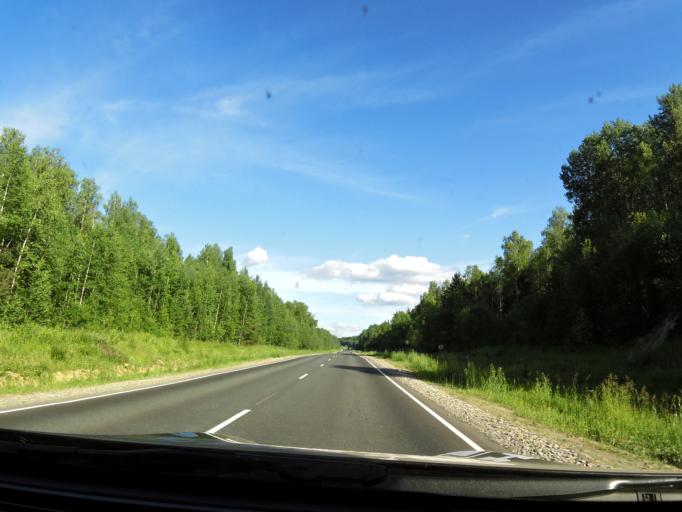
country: RU
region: Kirov
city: Chernaya Kholunitsa
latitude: 58.7830
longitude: 51.9080
